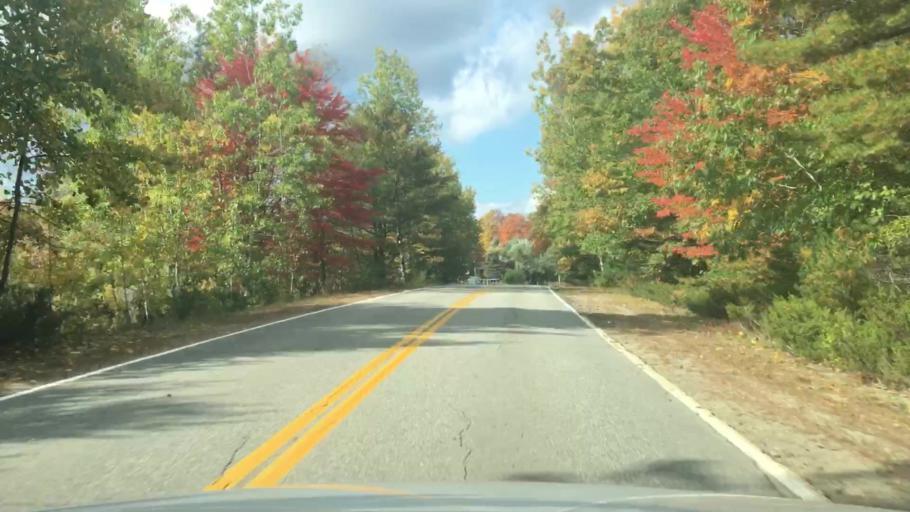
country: US
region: Maine
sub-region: Knox County
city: Washington
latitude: 44.3134
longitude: -69.3527
